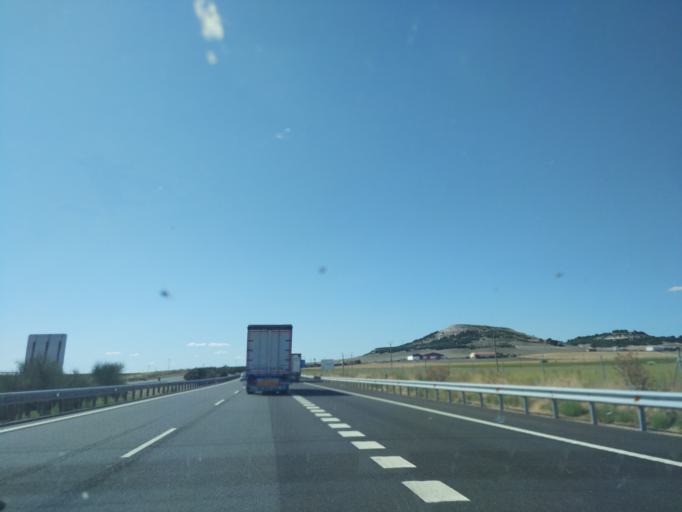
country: ES
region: Castille and Leon
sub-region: Provincia de Valladolid
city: Tordesillas
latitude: 41.5187
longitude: -5.0318
